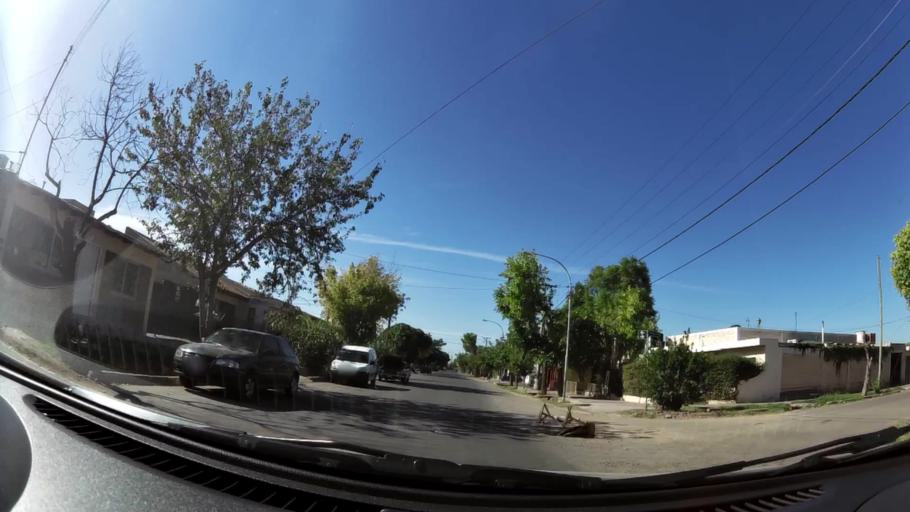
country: AR
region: Mendoza
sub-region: Departamento de Godoy Cruz
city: Godoy Cruz
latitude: -32.9445
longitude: -68.8107
